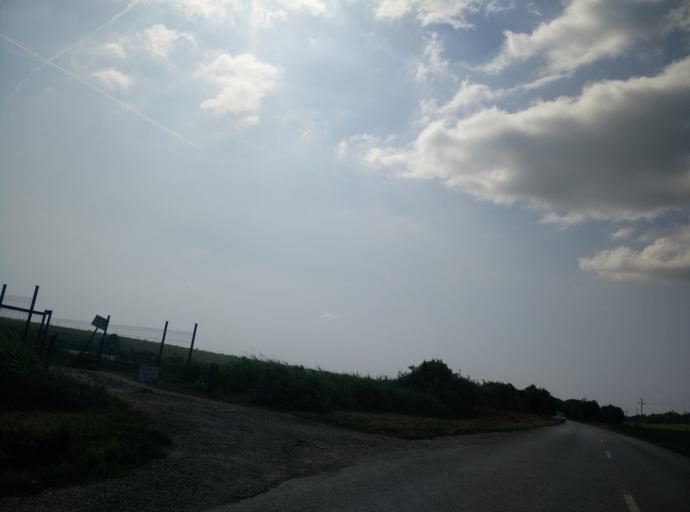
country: HU
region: Pest
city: Biatorbagy
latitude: 47.4791
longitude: 18.7880
